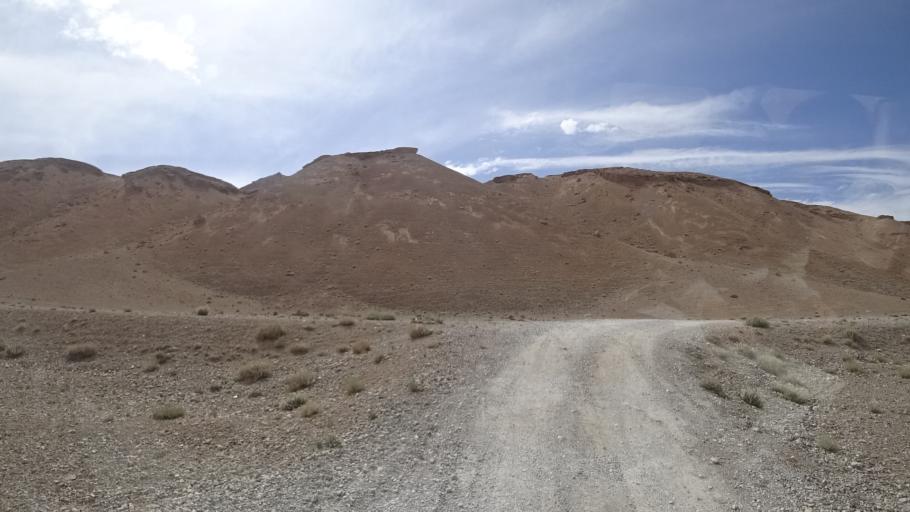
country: TJ
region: Gorno-Badakhshan
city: Murghob
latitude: 37.9753
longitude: 73.9571
